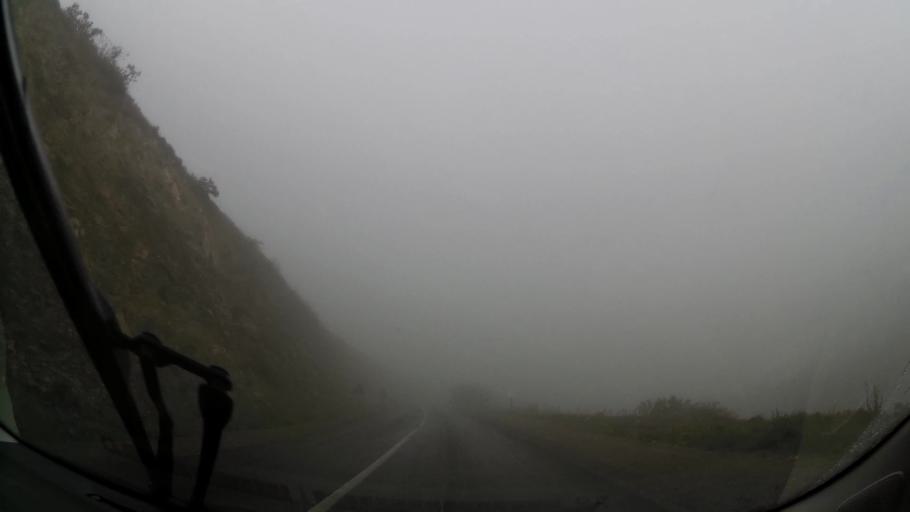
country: MA
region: Oriental
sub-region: Nador
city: Boudinar
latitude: 35.0953
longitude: -3.5352
